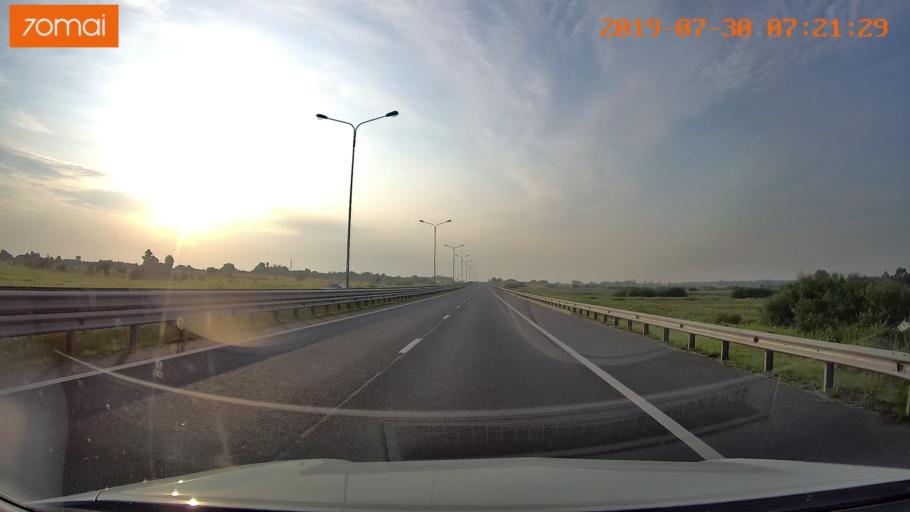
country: RU
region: Kaliningrad
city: Bol'shoe Isakovo
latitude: 54.6961
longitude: 20.7301
